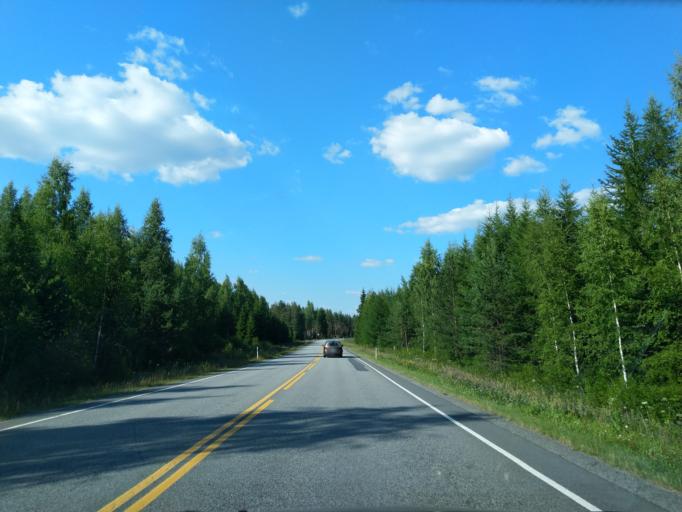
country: FI
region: Pirkanmaa
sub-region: Luoteis-Pirkanmaa
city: Kihnioe
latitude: 62.1399
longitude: 23.1455
